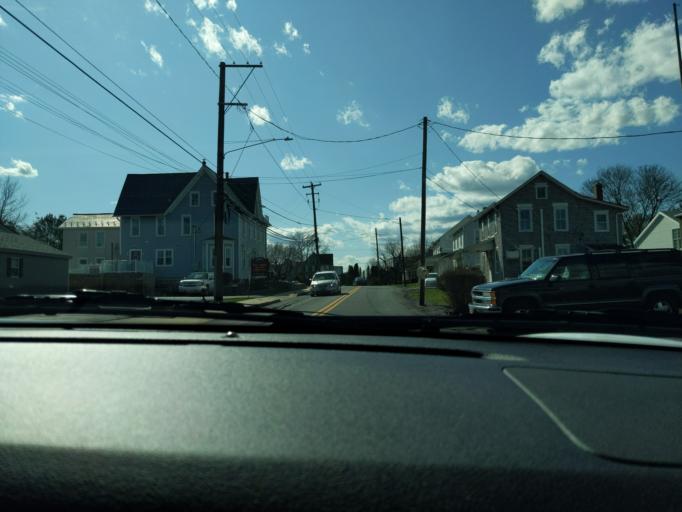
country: US
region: Pennsylvania
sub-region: Bucks County
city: Spinnerstown
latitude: 40.4370
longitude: -75.3996
